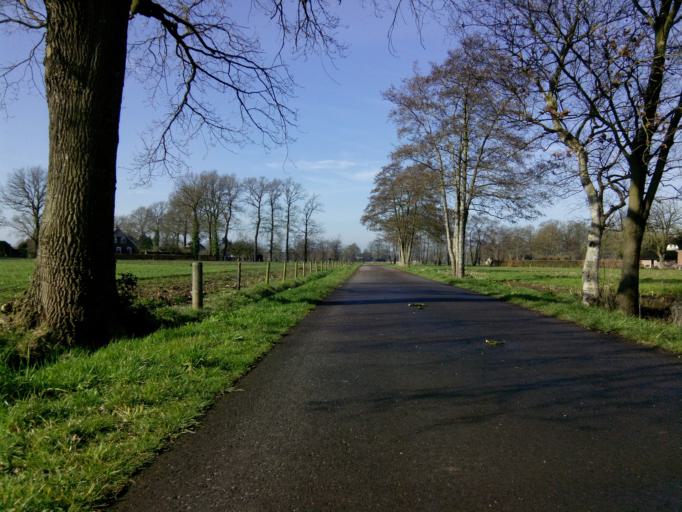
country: NL
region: Gelderland
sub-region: Gemeente Barneveld
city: Kootwijkerbroek
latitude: 52.1525
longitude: 5.6954
